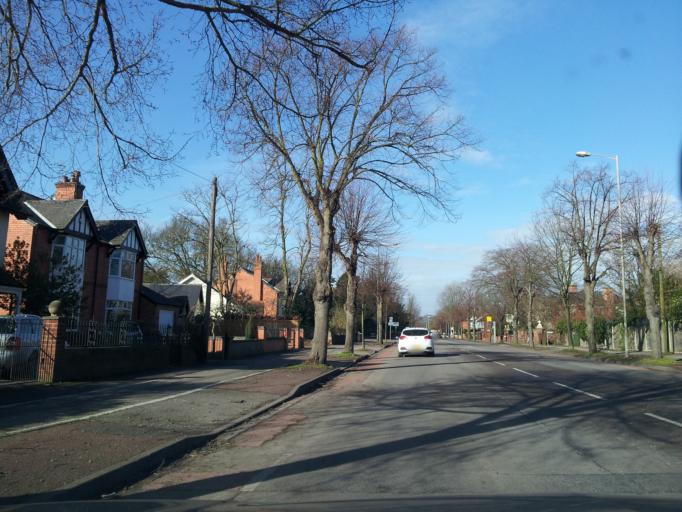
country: GB
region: England
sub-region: Nottinghamshire
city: Newark on Trent
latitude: 53.0684
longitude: -0.7970
